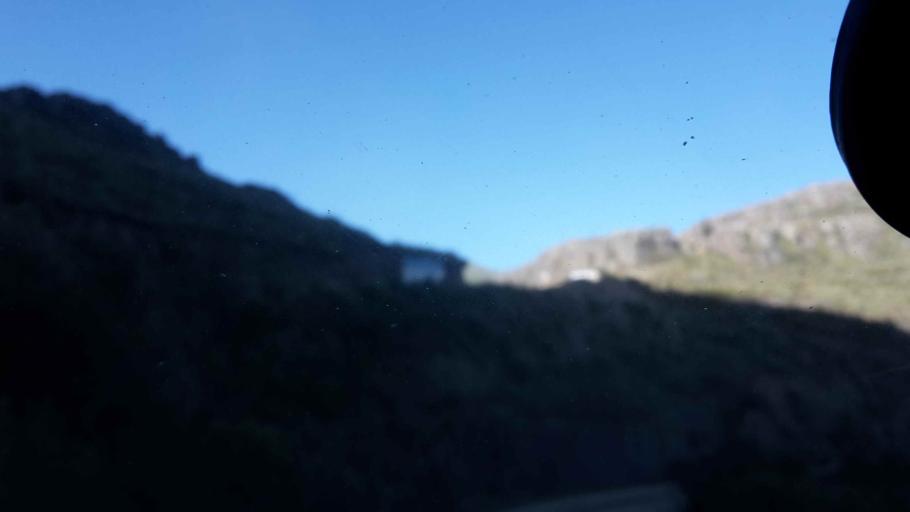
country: BO
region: Cochabamba
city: Arani
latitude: -17.7265
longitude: -65.6324
